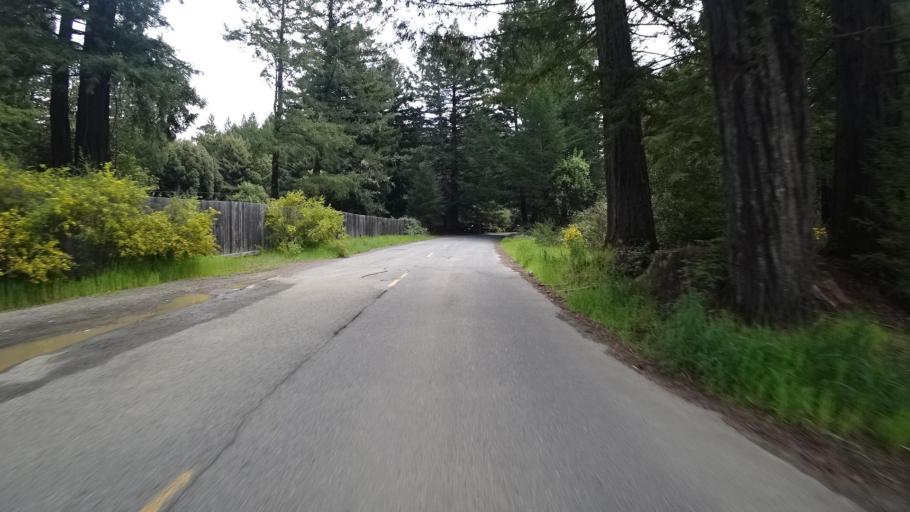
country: US
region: California
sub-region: Humboldt County
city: Redway
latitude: 40.0222
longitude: -123.9390
